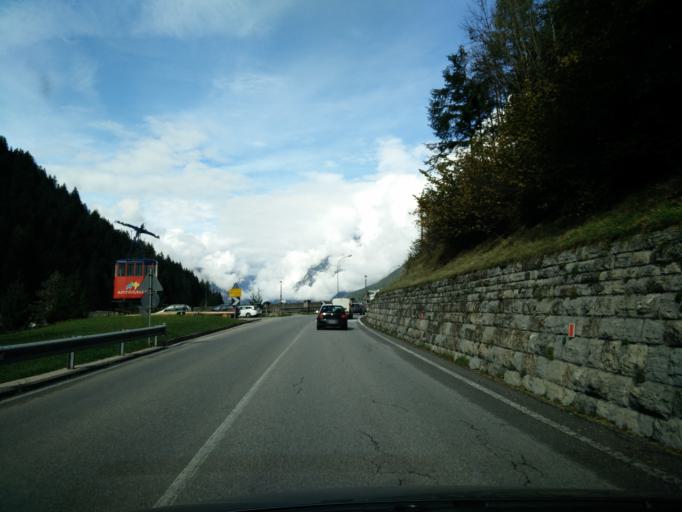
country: IT
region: Veneto
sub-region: Provincia di Belluno
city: Vigo di Cadore
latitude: 46.5387
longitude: 12.4645
